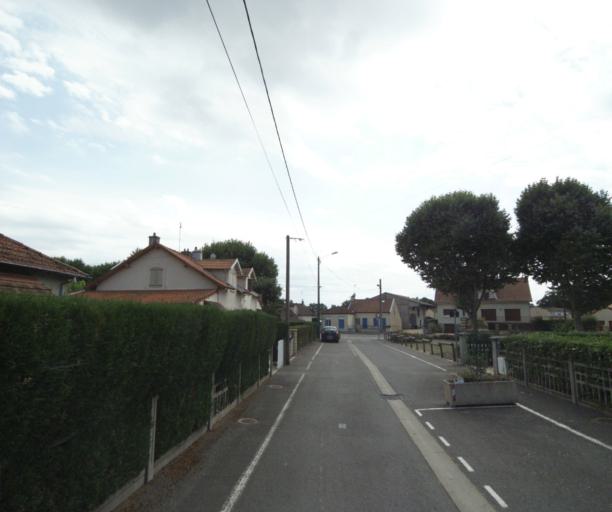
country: FR
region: Bourgogne
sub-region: Departement de Saone-et-Loire
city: Gueugnon
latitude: 46.6074
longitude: 4.0490
